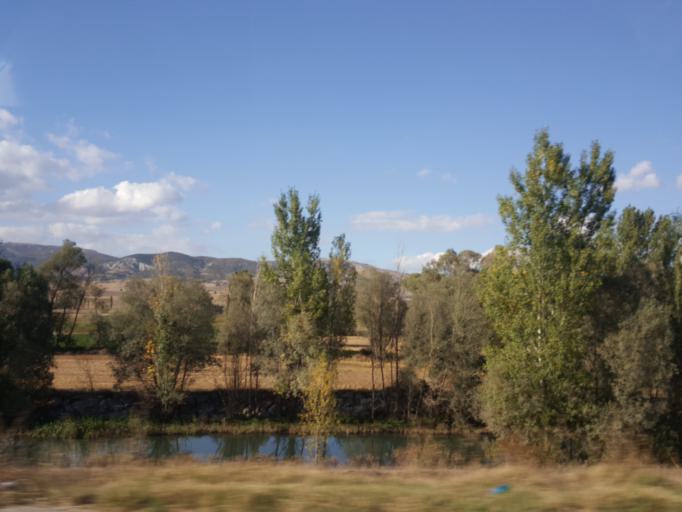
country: TR
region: Tokat
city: Yesilyurt
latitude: 40.0154
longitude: 36.2394
